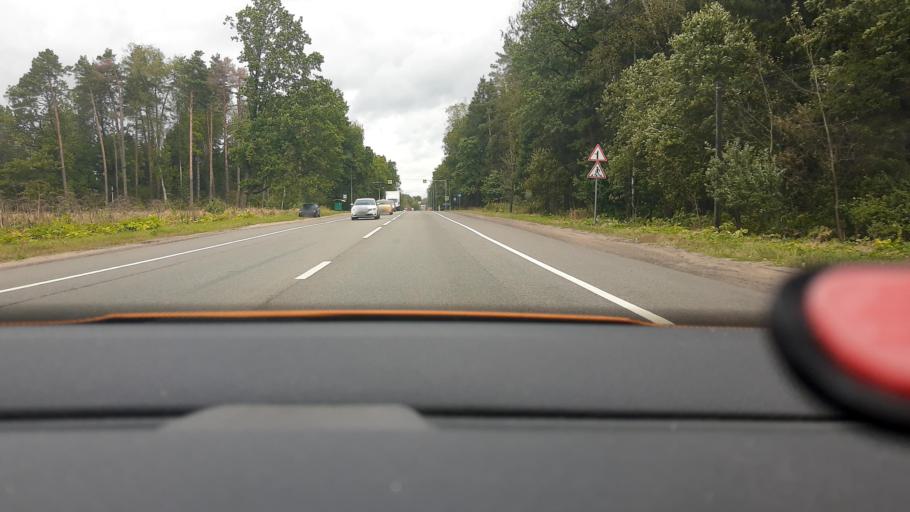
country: RU
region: Moskovskaya
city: Kostino
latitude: 56.0363
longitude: 37.9687
